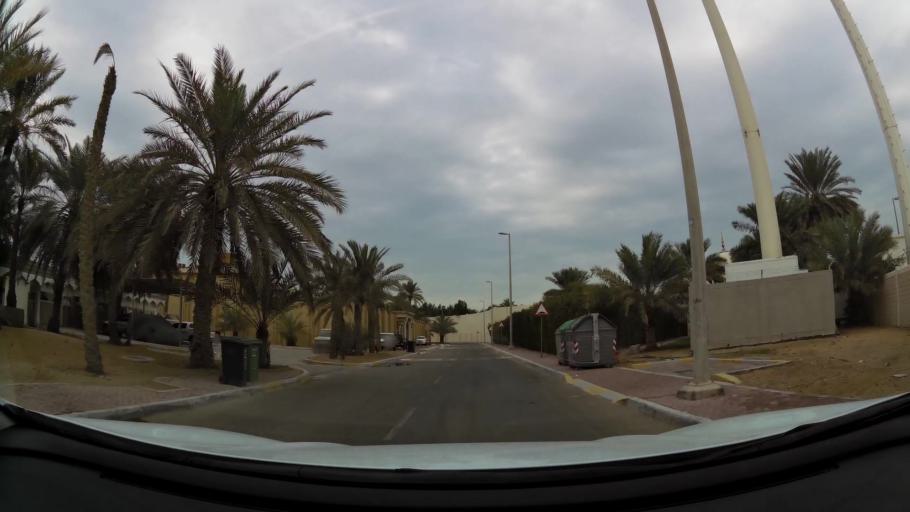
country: AE
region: Abu Dhabi
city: Abu Dhabi
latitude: 24.4358
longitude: 54.3854
